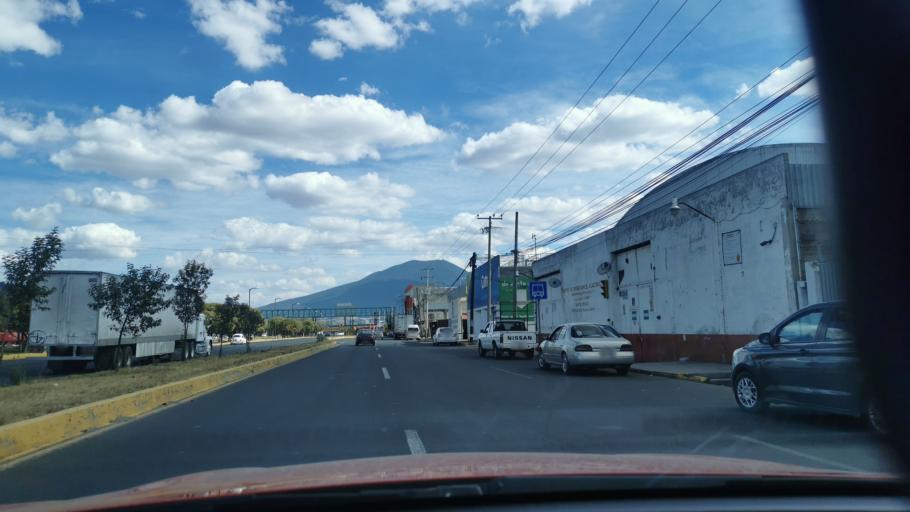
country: MX
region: Mexico
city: Atlacomulco
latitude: 19.7882
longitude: -99.8781
